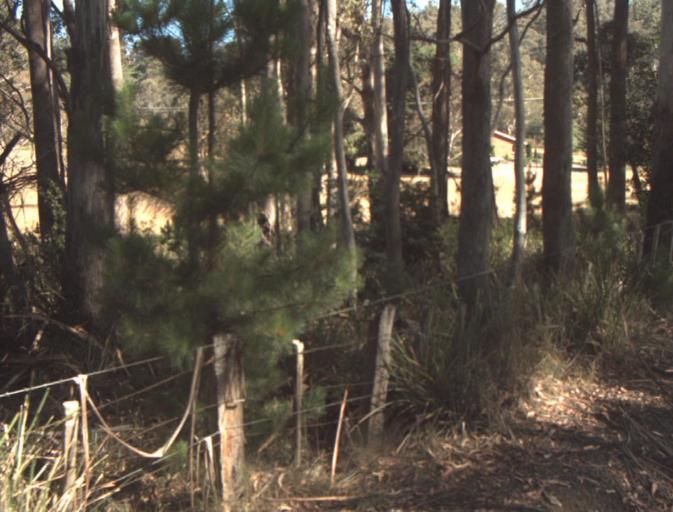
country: AU
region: Tasmania
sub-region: Launceston
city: Newstead
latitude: -41.3292
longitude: 147.3429
